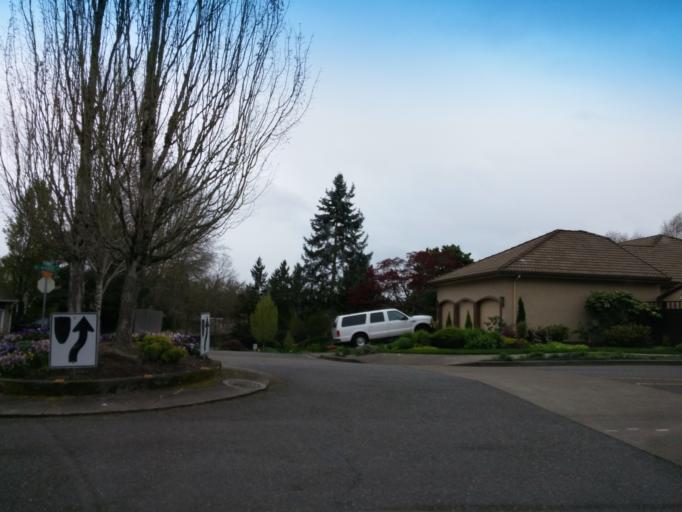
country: US
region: Oregon
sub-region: Washington County
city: Oak Hills
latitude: 45.5231
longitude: -122.8442
